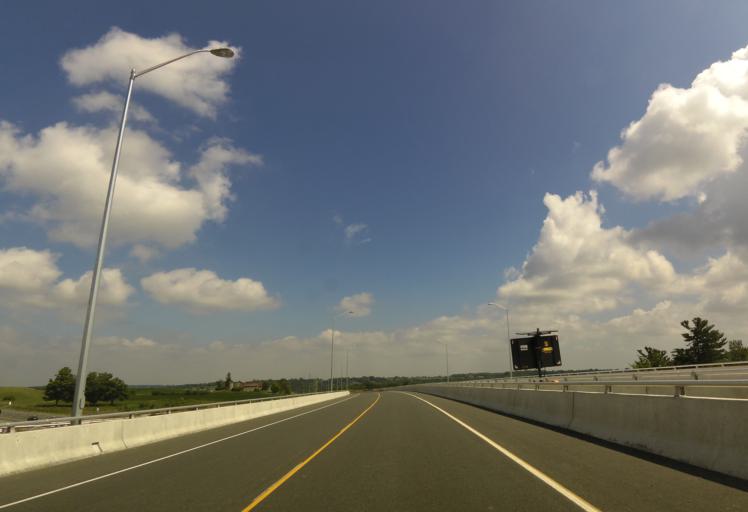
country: CA
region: Ontario
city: Pickering
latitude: 43.9223
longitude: -79.0946
